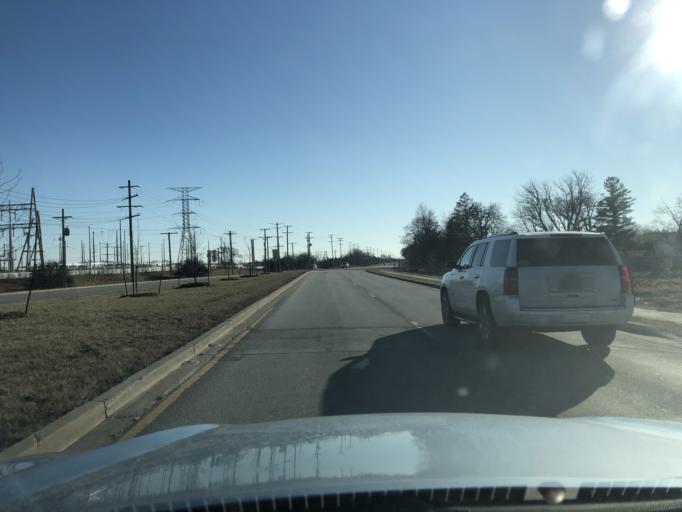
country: US
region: Illinois
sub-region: DuPage County
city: Itasca
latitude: 41.9821
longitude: -87.9983
